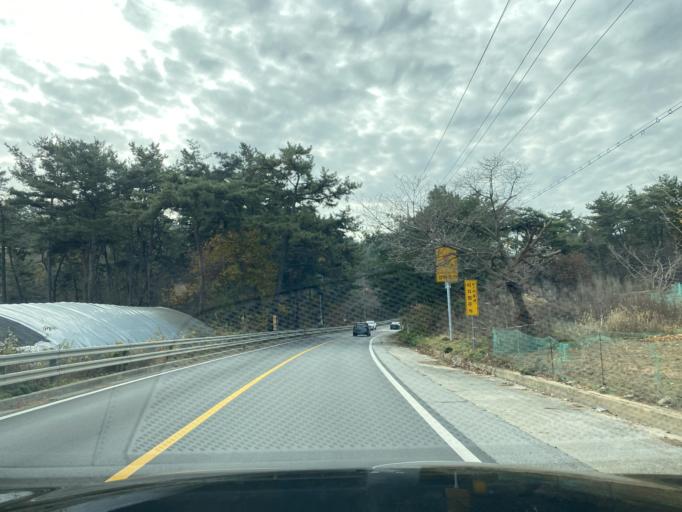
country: KR
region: Chungcheongnam-do
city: Hongsung
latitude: 36.6728
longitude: 126.6424
